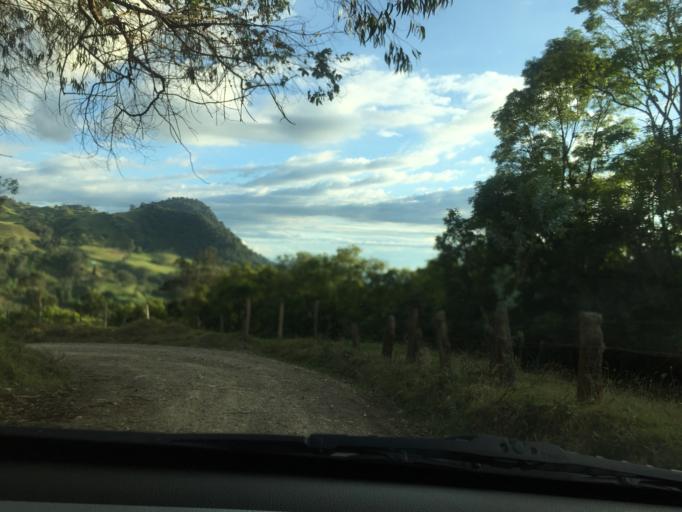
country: CO
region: Cundinamarca
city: Zipacon
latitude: 4.7286
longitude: -74.3909
